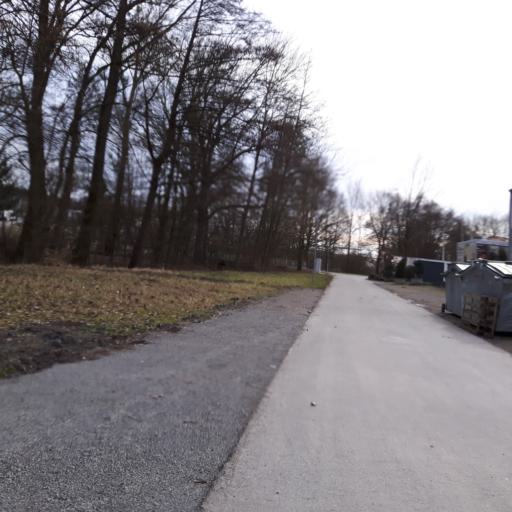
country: DE
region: Baden-Wuerttemberg
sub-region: Regierungsbezirk Stuttgart
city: Grossbottwar
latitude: 49.0055
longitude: 9.3037
